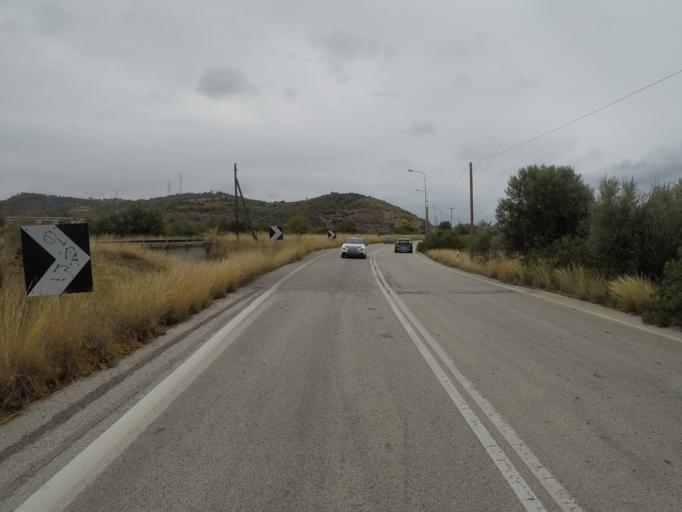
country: GR
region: Peloponnese
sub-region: Nomos Korinthias
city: Agioi Theodoroi
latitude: 37.9194
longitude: 23.0934
